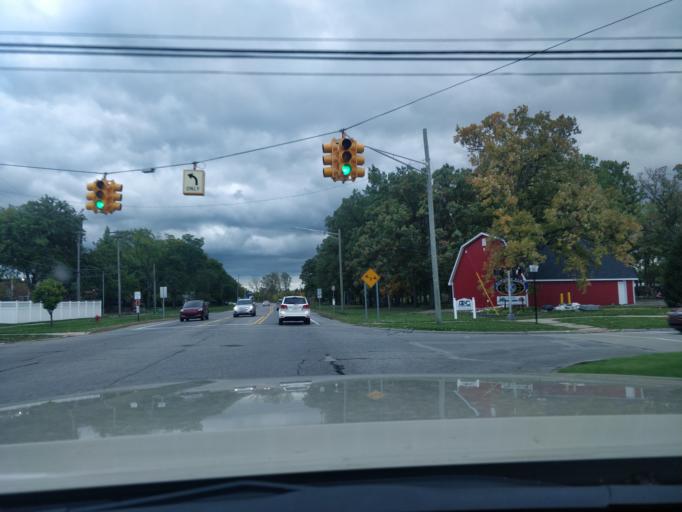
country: US
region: Michigan
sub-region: Wayne County
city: Southgate
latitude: 42.1922
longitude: -83.1933
